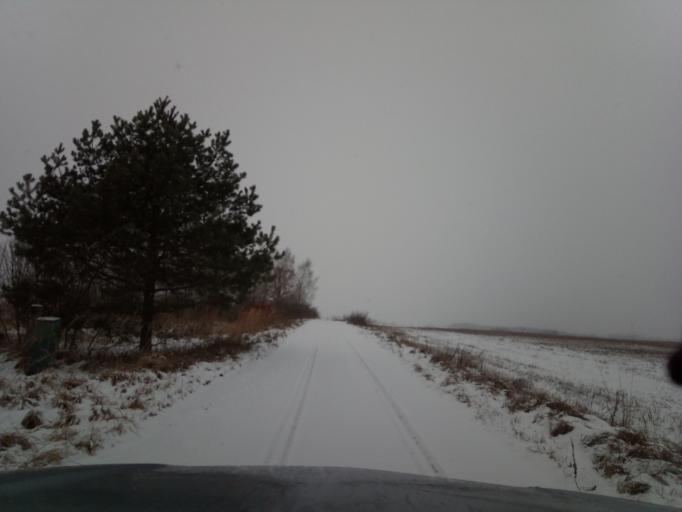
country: LT
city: Ramygala
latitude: 55.5874
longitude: 24.3679
